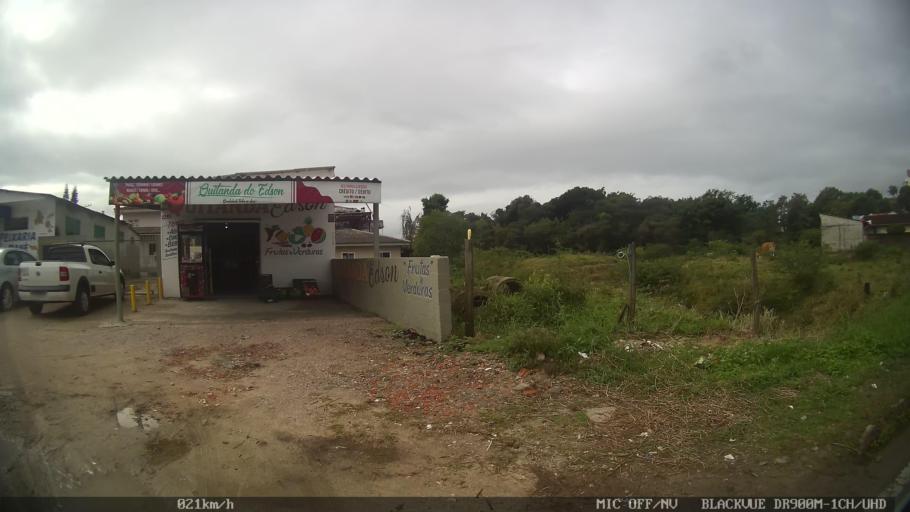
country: BR
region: Santa Catarina
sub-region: Biguacu
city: Biguacu
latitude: -27.5276
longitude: -48.6458
